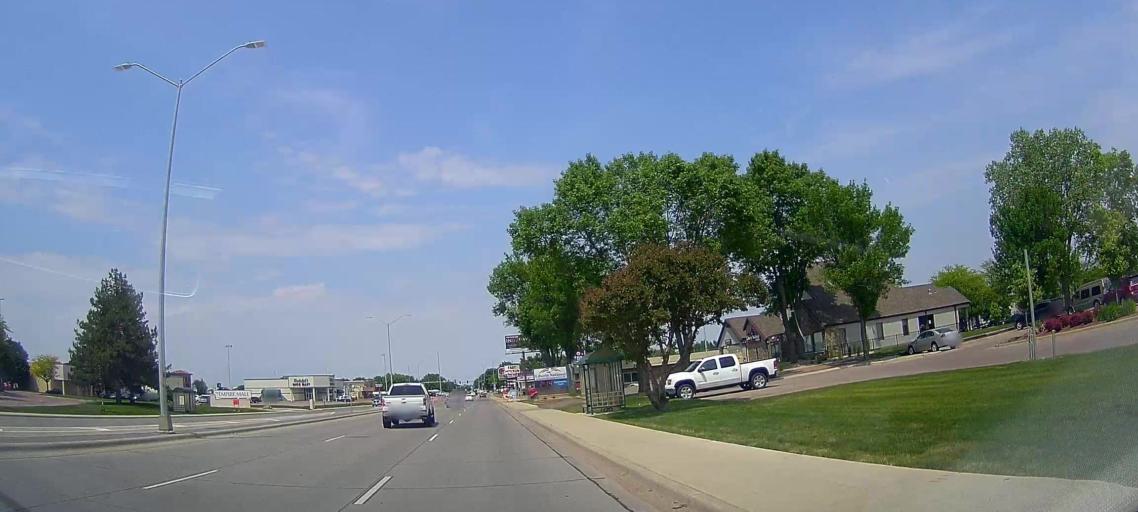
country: US
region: South Dakota
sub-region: Minnehaha County
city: Sioux Falls
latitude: 43.5122
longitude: -96.7710
